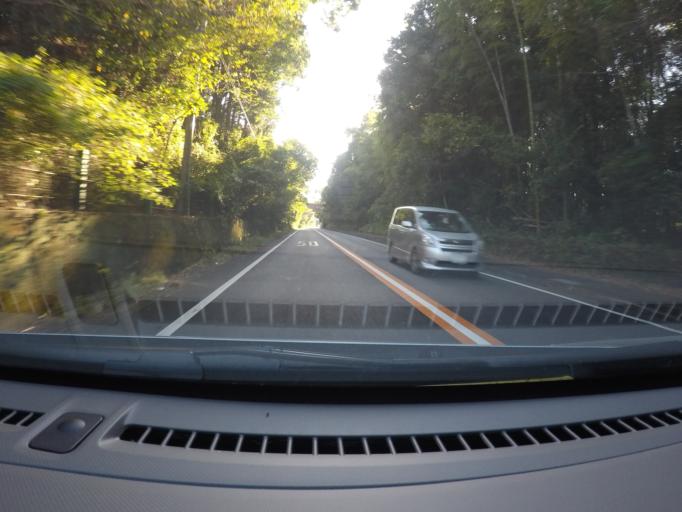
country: JP
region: Kumamoto
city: Minamata
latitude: 32.1694
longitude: 130.3794
